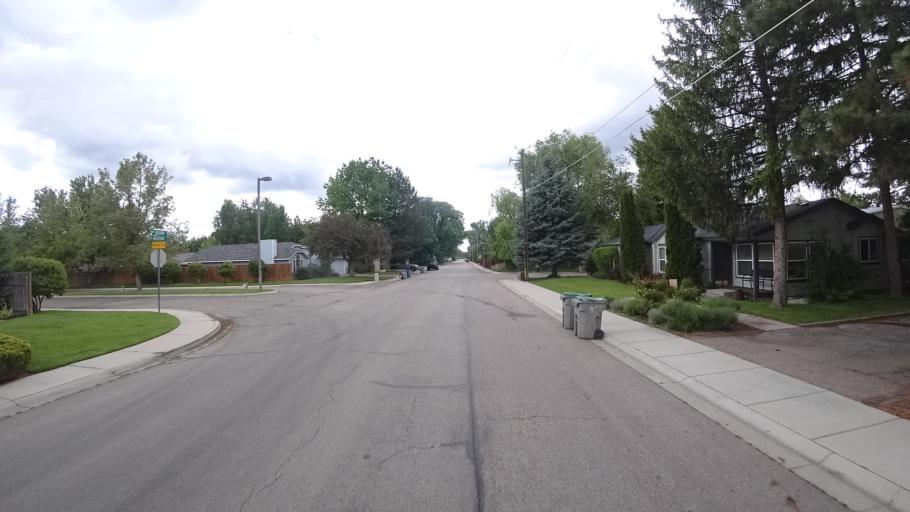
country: US
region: Idaho
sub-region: Ada County
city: Garden City
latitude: 43.6574
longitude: -116.2504
